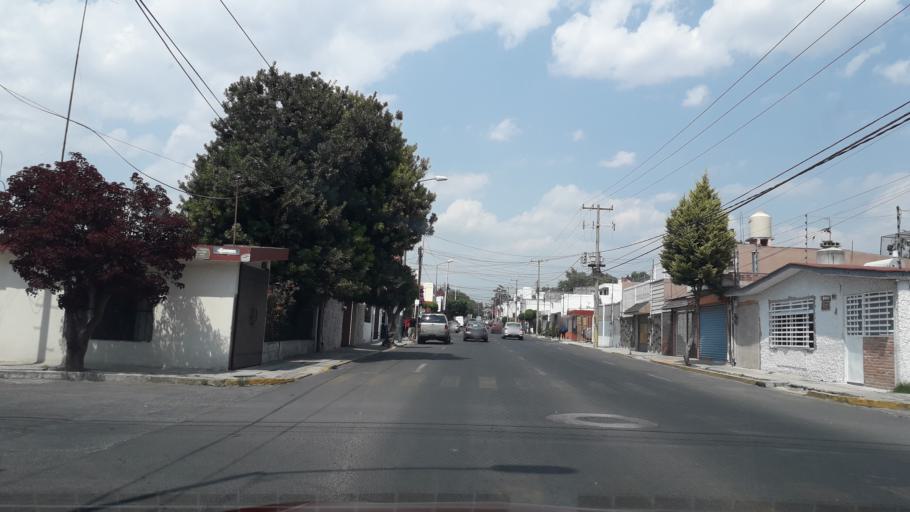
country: MX
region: Puebla
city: Puebla
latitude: 19.0344
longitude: -98.2200
